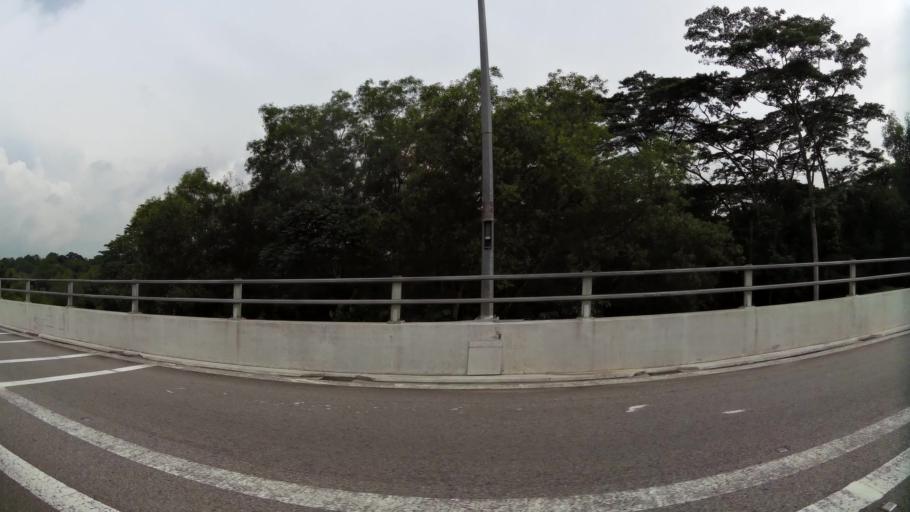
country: MY
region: Johor
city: Johor Bahru
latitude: 1.4184
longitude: 103.7682
